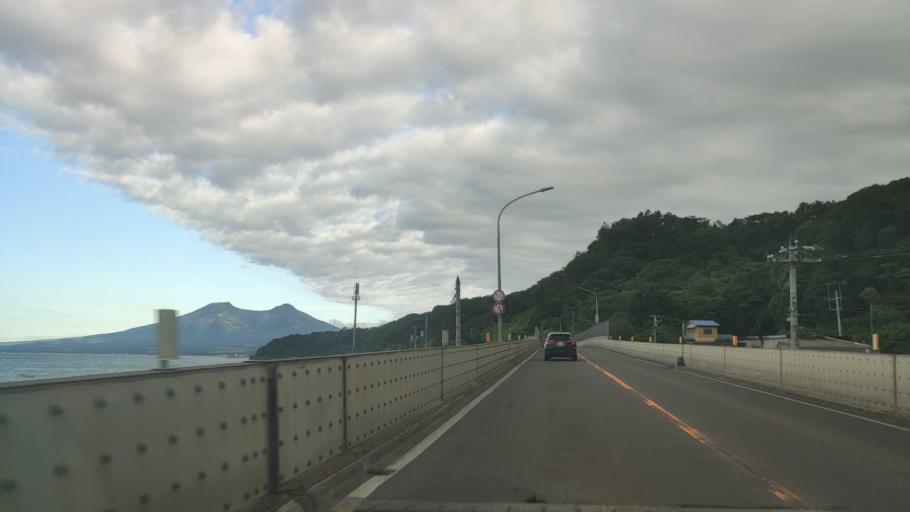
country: JP
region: Hokkaido
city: Nanae
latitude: 42.1290
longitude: 140.5141
